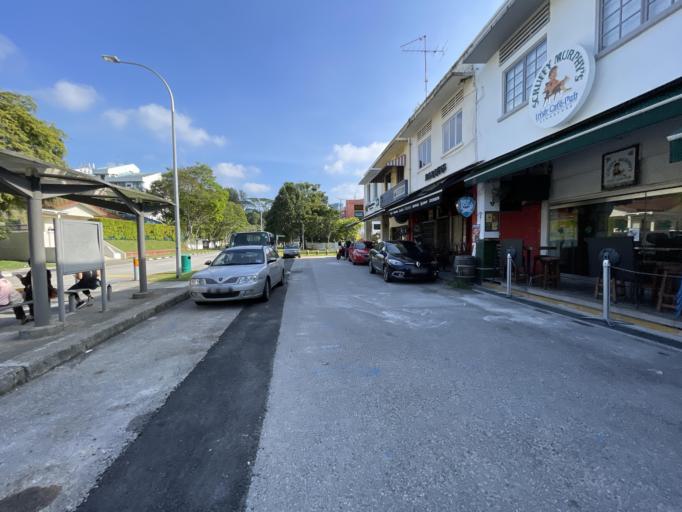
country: SG
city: Singapore
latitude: 1.2807
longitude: 103.7868
